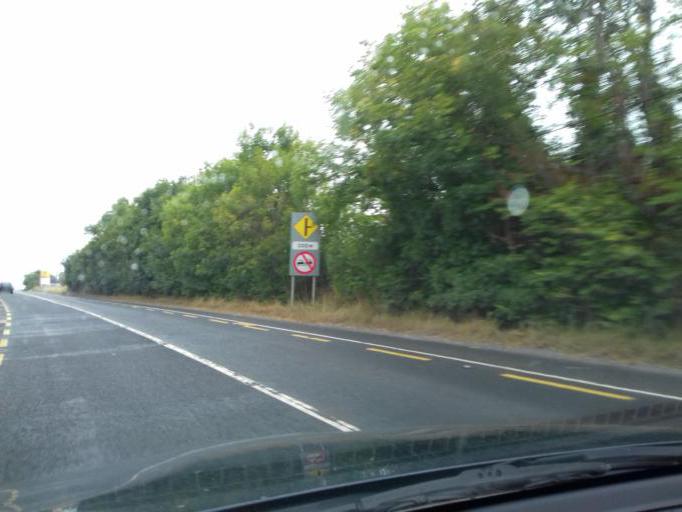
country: IE
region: Leinster
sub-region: County Carlow
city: Bagenalstown
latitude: 52.7568
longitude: -6.9575
